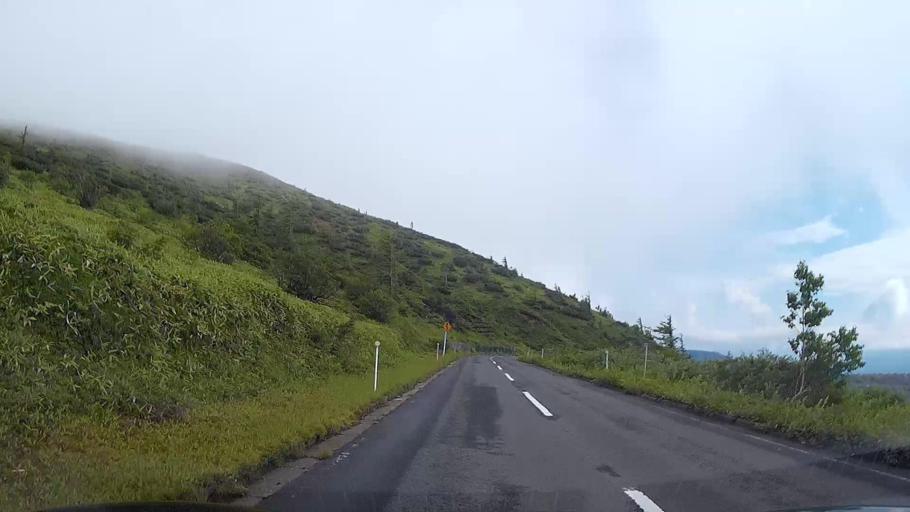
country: JP
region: Nagano
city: Nakano
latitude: 36.6473
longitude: 138.5254
